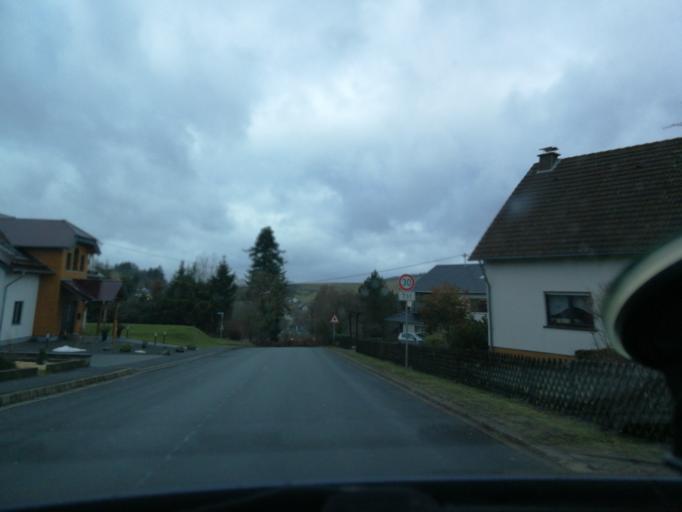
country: DE
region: Rheinland-Pfalz
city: Dreis-Bruck
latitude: 50.2612
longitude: 6.7960
